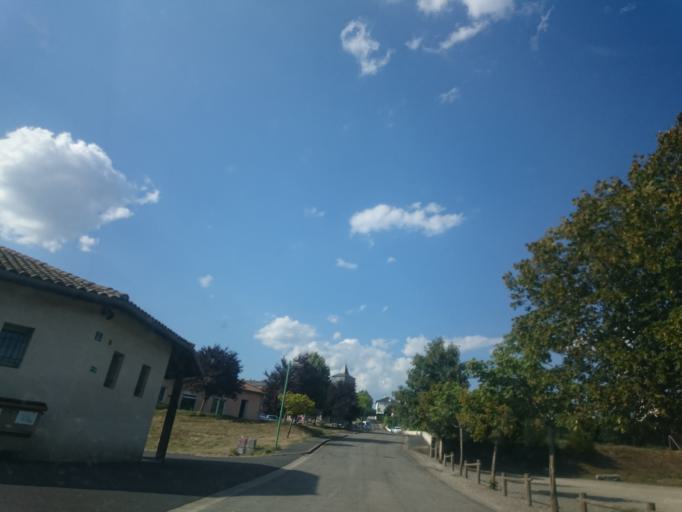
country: FR
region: Auvergne
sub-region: Departement du Cantal
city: Saint-Mamet-la-Salvetat
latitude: 44.8521
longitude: 2.2327
